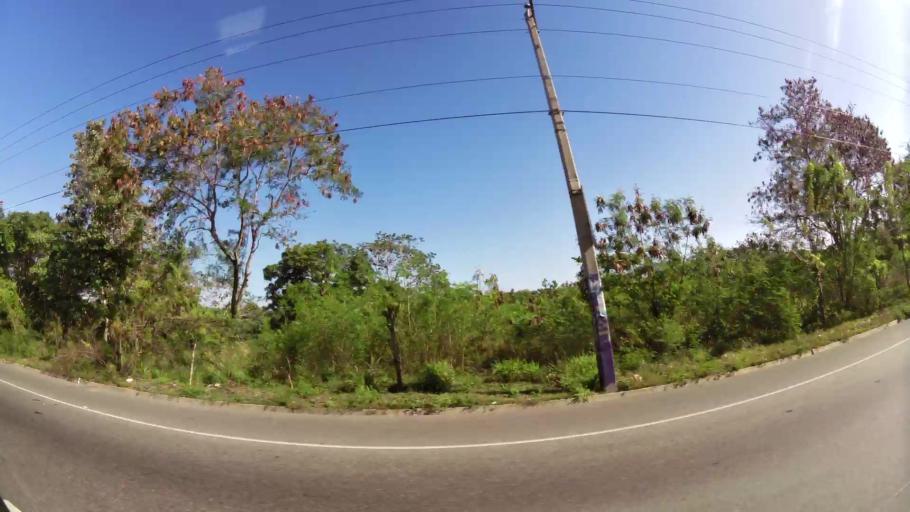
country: DO
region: San Cristobal
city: San Cristobal
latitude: 18.4336
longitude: -70.0744
